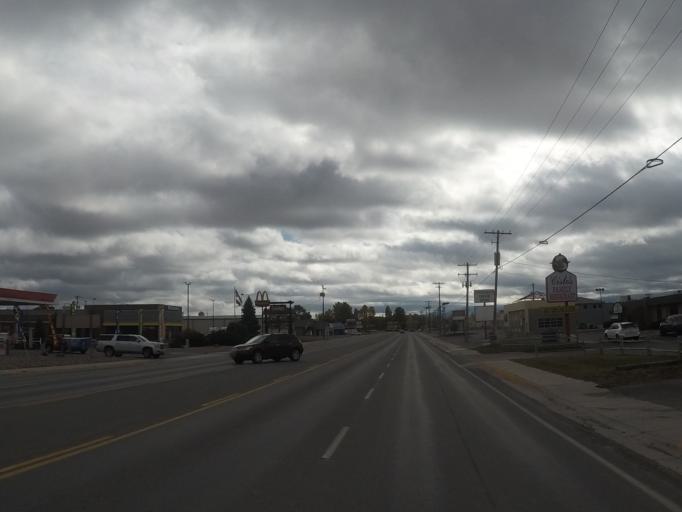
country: US
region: Montana
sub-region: Flathead County
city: Evergreen
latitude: 48.2183
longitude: -114.2774
